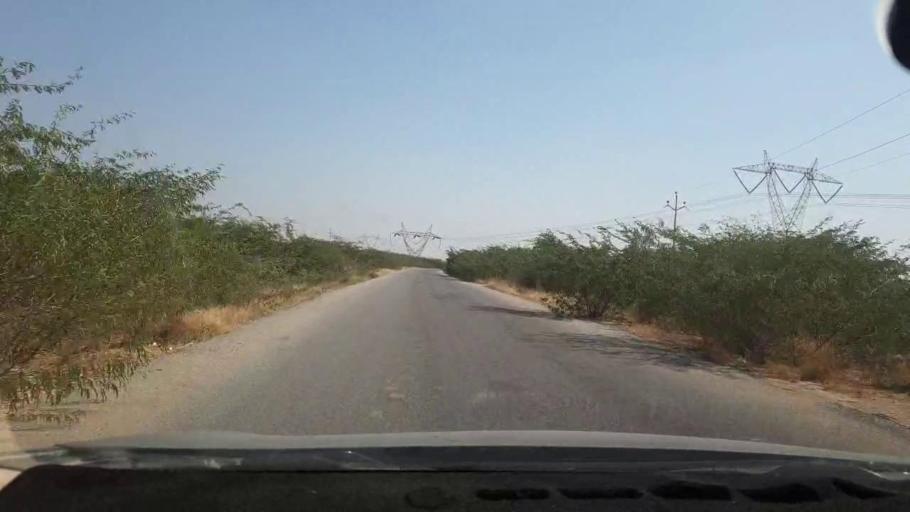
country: PK
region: Sindh
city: Malir Cantonment
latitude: 25.1441
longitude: 67.1905
